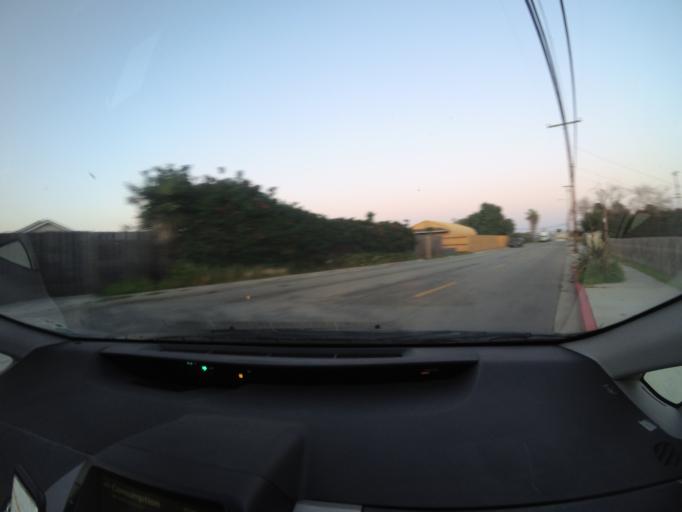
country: US
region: California
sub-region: San Diego County
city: Imperial Beach
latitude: 32.5801
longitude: -117.1165
